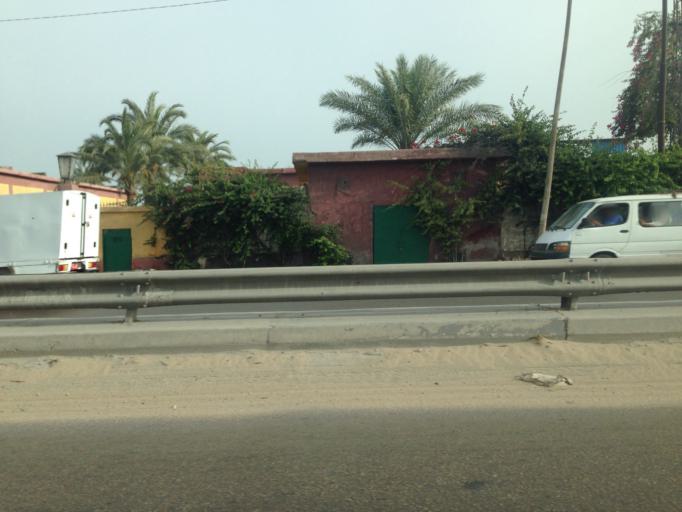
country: EG
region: Alexandria
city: Alexandria
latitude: 31.2035
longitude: 30.0099
